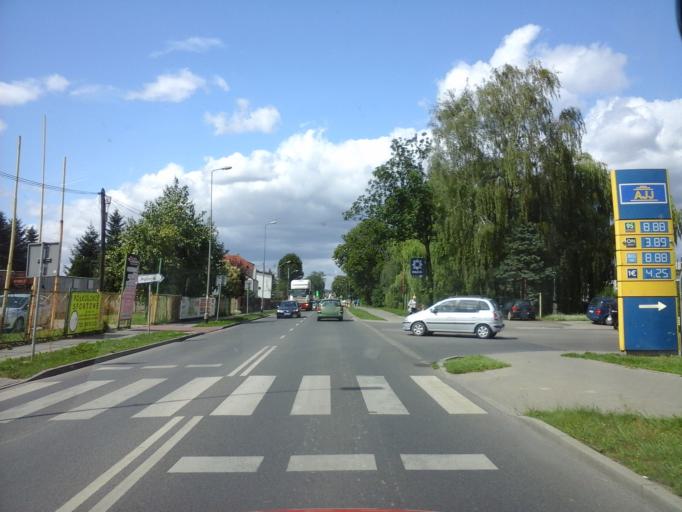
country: PL
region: West Pomeranian Voivodeship
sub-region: Powiat policki
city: Przeclaw
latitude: 53.4285
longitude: 14.4719
